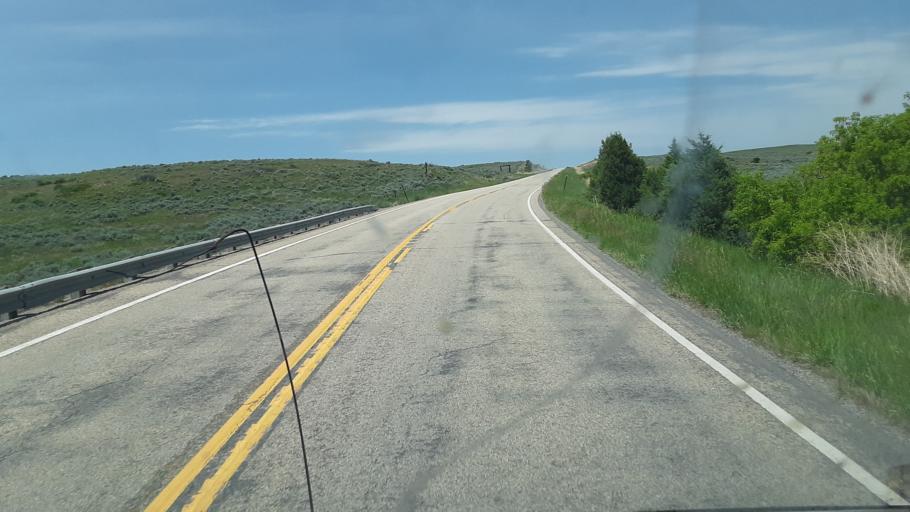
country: US
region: Montana
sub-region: Stillwater County
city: Columbus
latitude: 45.4787
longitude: -109.0062
